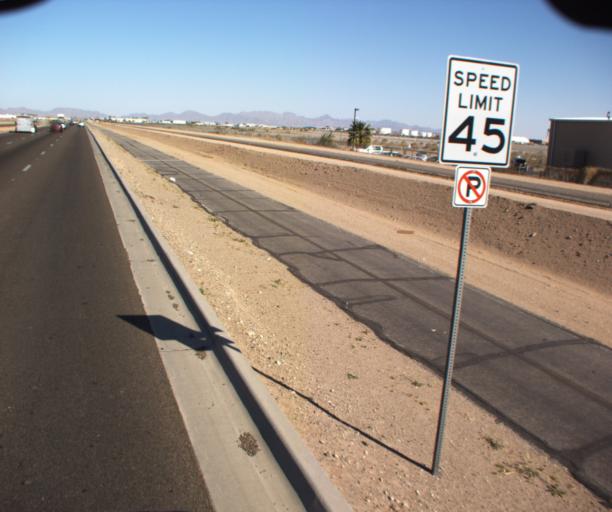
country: US
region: Arizona
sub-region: Yuma County
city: Yuma
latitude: 32.6693
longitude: -114.5975
